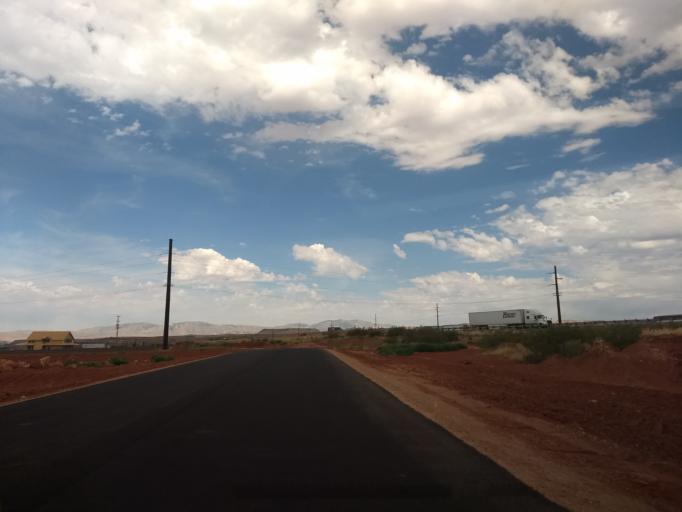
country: US
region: Utah
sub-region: Washington County
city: Washington
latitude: 37.1436
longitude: -113.4939
